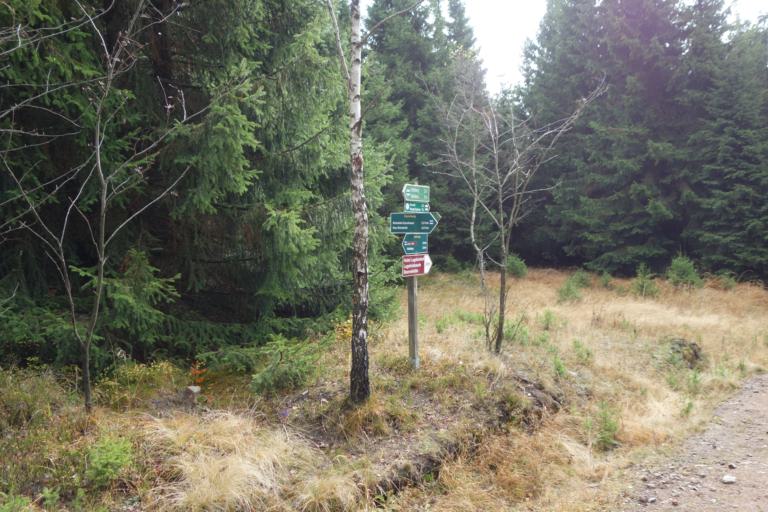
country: DE
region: Saxony
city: Altenberg
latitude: 50.7370
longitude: 13.7292
